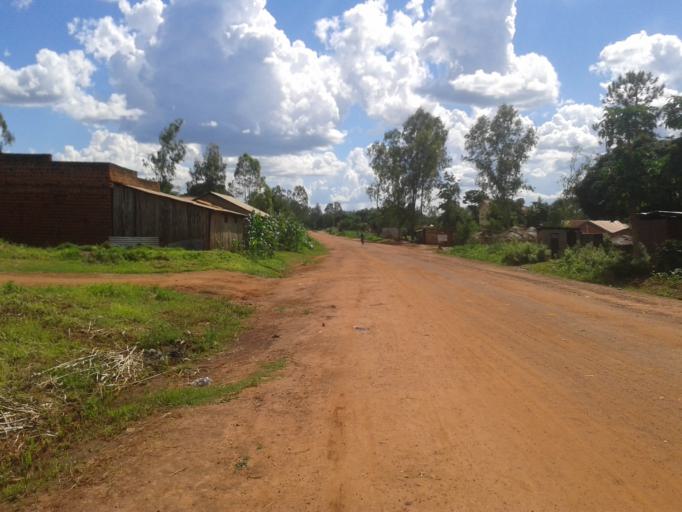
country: UG
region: Northern Region
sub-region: Gulu District
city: Gulu
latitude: 2.7584
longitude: 32.3142
